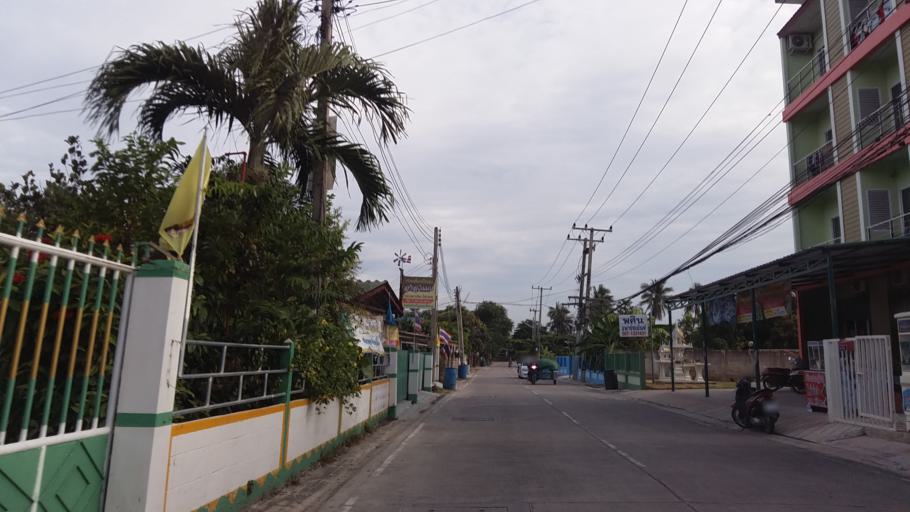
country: TH
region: Chon Buri
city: Chon Buri
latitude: 13.3091
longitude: 100.9381
